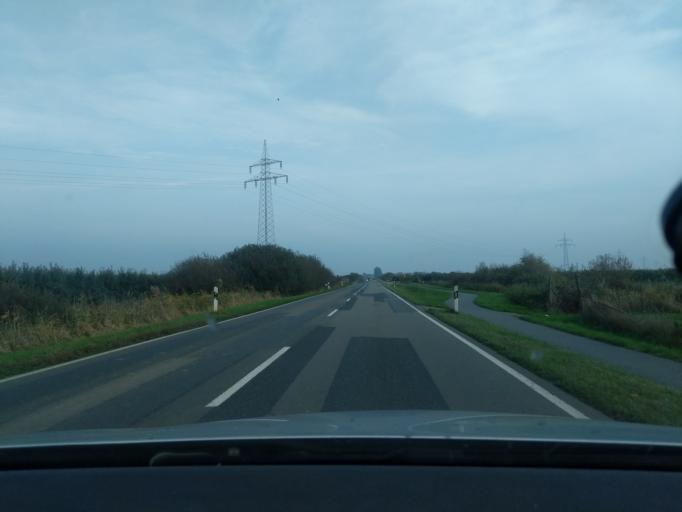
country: DE
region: Lower Saxony
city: Guderhandviertel
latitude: 53.5457
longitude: 9.5834
